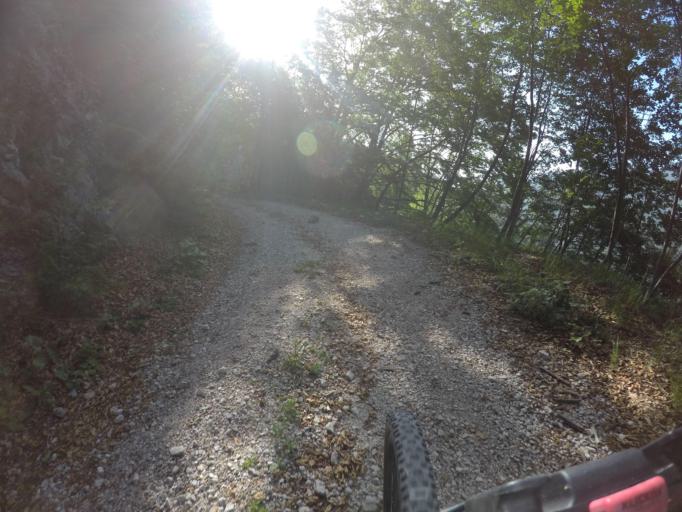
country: IT
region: Friuli Venezia Giulia
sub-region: Provincia di Udine
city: Resiutta
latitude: 46.3340
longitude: 13.2113
